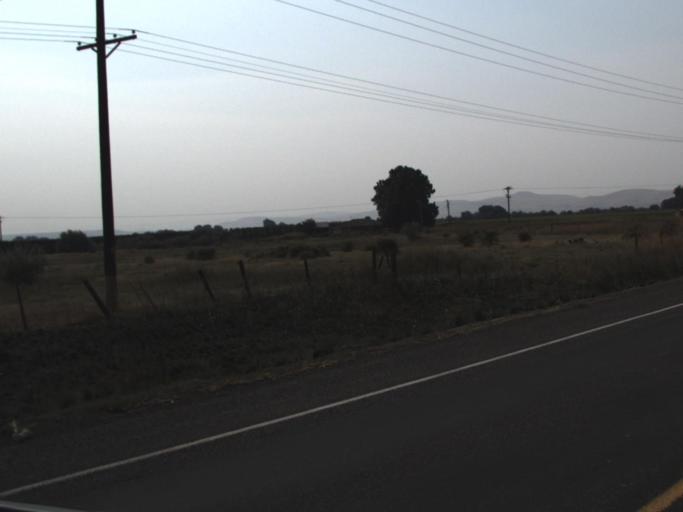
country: US
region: Washington
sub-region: Yakima County
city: Granger
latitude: 46.2662
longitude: -120.1438
